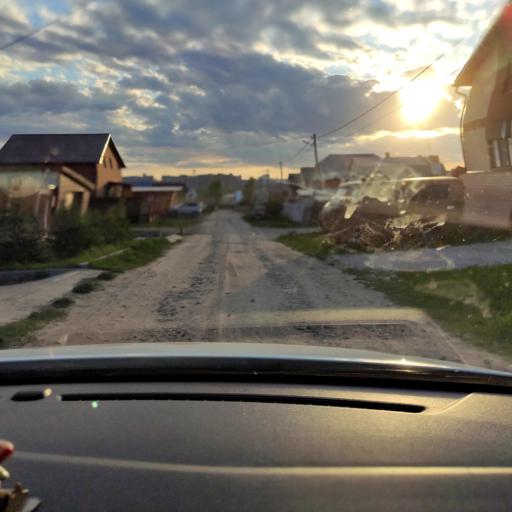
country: RU
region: Tatarstan
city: Vysokaya Gora
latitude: 55.7808
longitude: 49.2678
